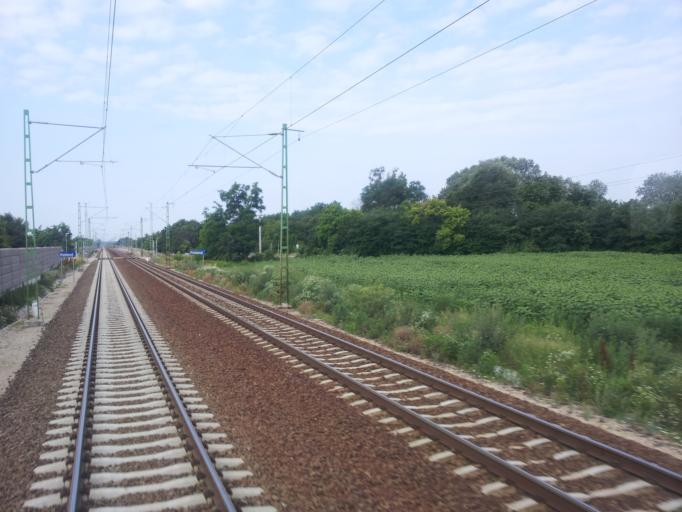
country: HU
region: Fejer
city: Baracska
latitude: 47.2659
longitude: 18.7169
